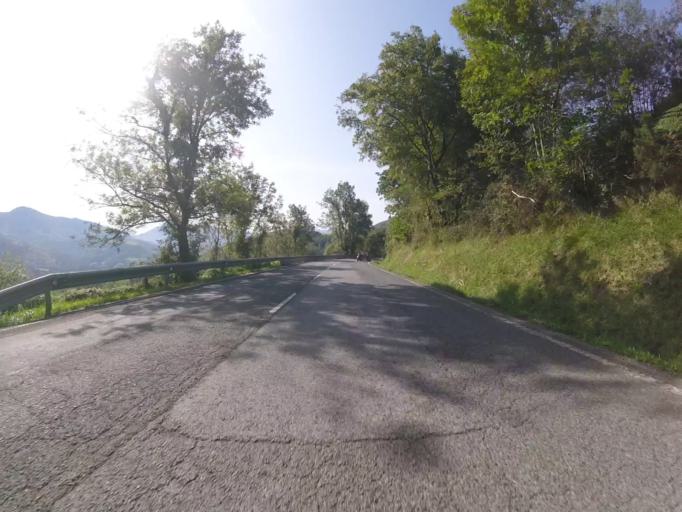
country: ES
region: Navarre
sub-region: Provincia de Navarra
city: Zugarramurdi
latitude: 43.2302
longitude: -1.4971
